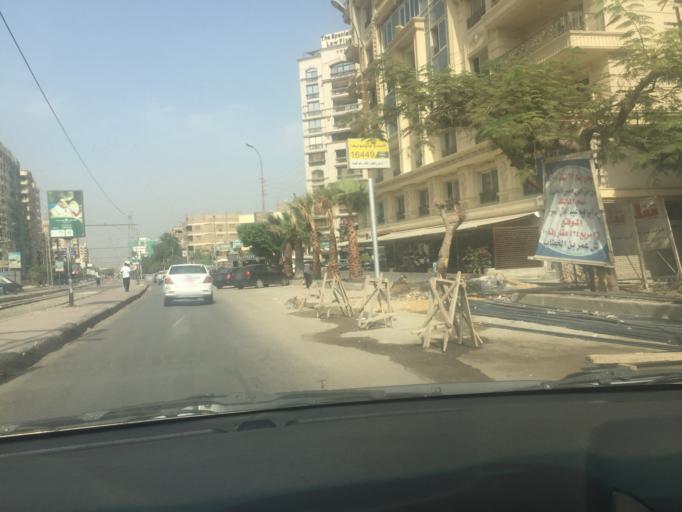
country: EG
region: Muhafazat al Qahirah
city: Cairo
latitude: 30.0871
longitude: 31.3465
